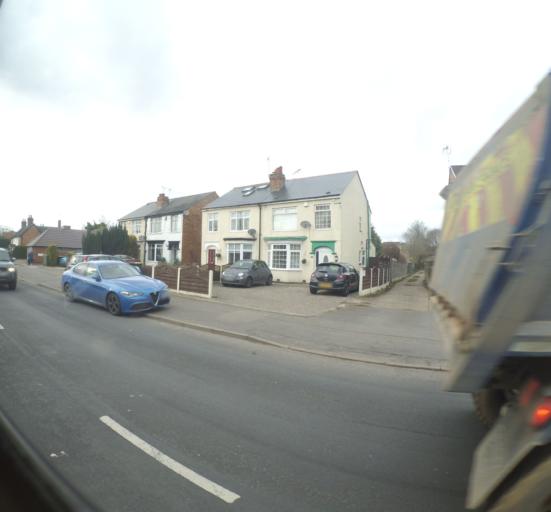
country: GB
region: England
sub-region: Warwickshire
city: Ryton on Dunsmore
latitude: 52.4042
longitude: -1.4417
